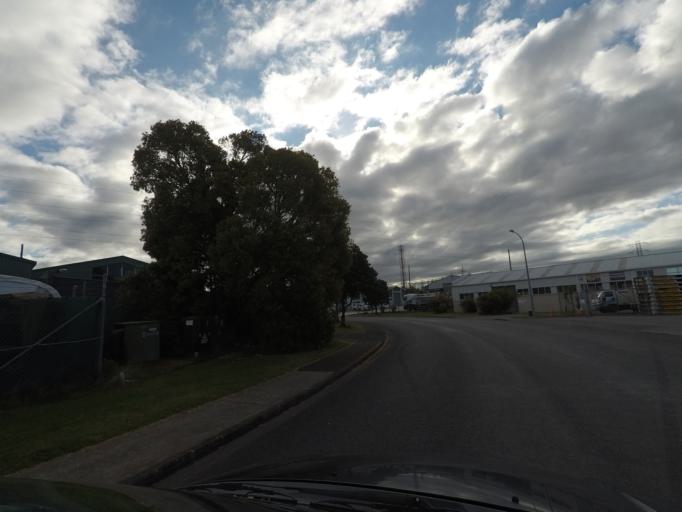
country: NZ
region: Auckland
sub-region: Auckland
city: Rosebank
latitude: -36.8863
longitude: 174.6631
